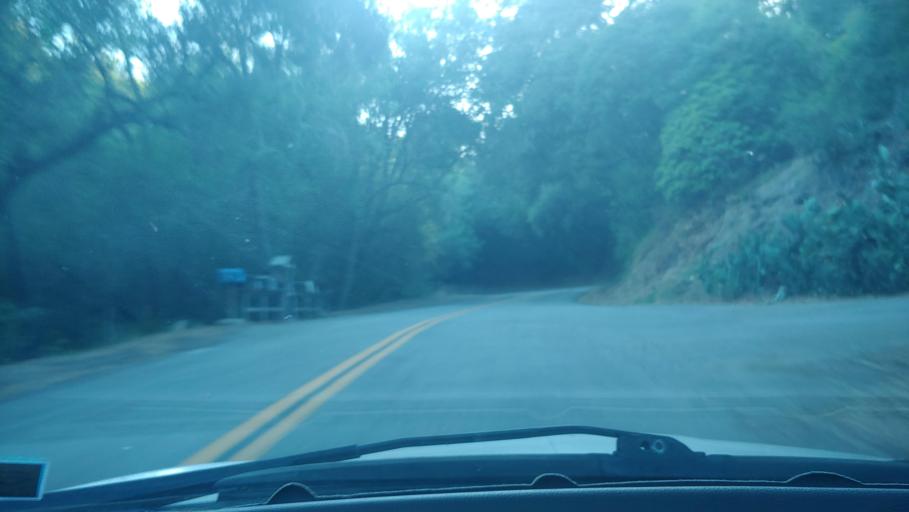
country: US
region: California
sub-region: Santa Barbara County
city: Goleta
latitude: 34.5156
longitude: -119.8303
